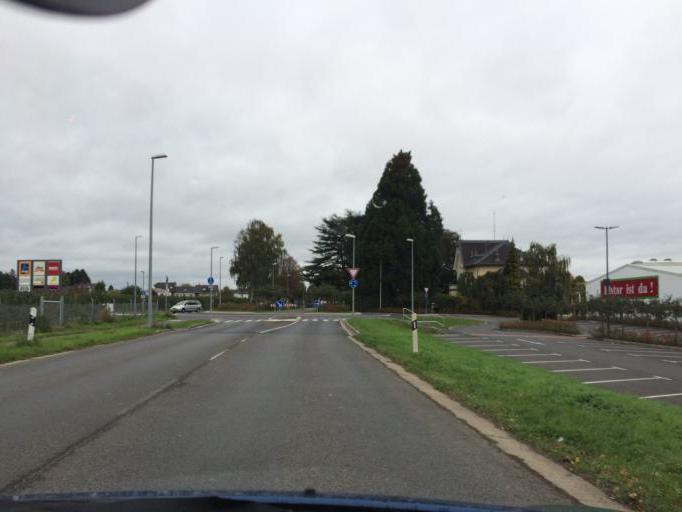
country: DE
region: North Rhine-Westphalia
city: Bruhl
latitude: 50.7759
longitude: 6.9299
